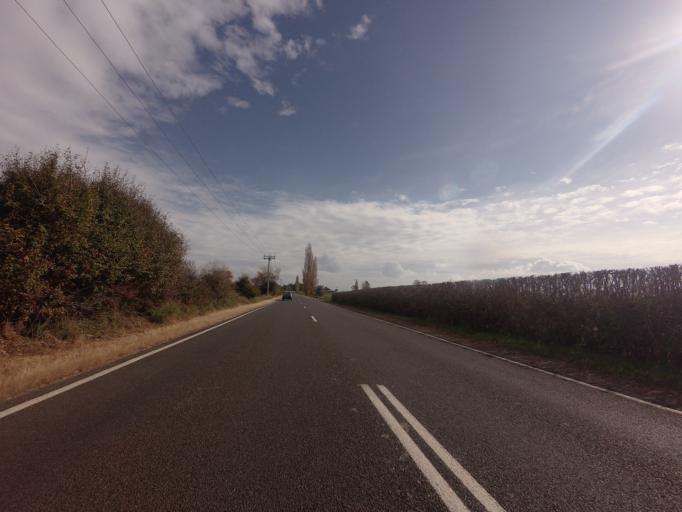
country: AU
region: Tasmania
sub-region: Meander Valley
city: Deloraine
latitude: -41.5248
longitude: 146.7105
